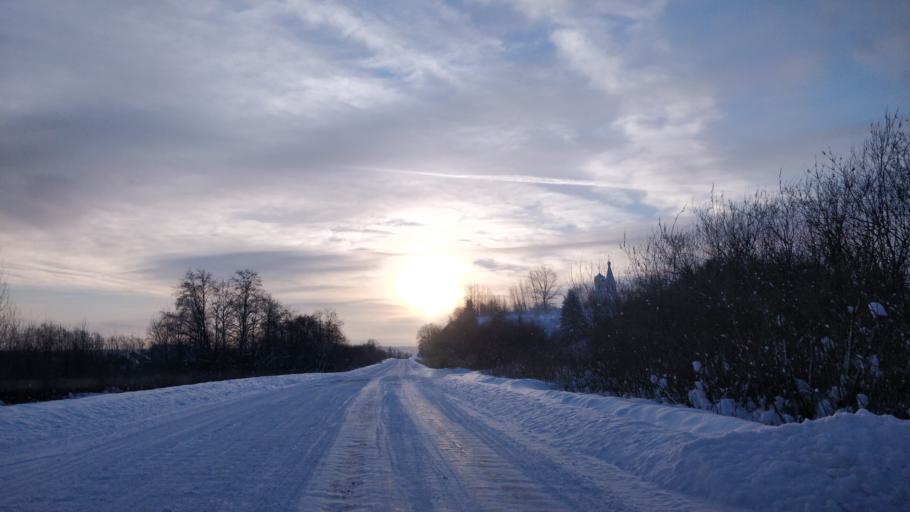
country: RU
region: Perm
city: Verkhnechusovskiye Gorodki
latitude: 58.2004
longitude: 57.1436
